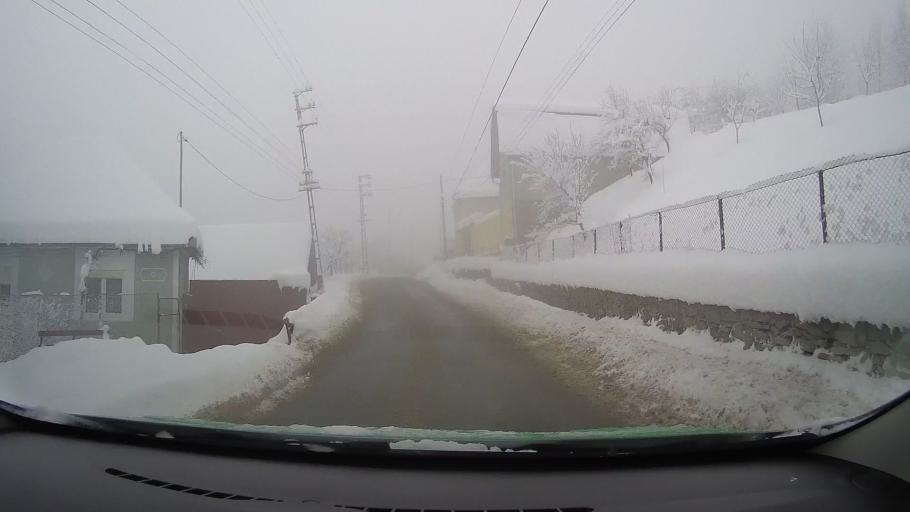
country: RO
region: Sibiu
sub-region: Comuna Poiana Sibiului
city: Poiana Sibiului
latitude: 45.8060
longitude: 23.7728
